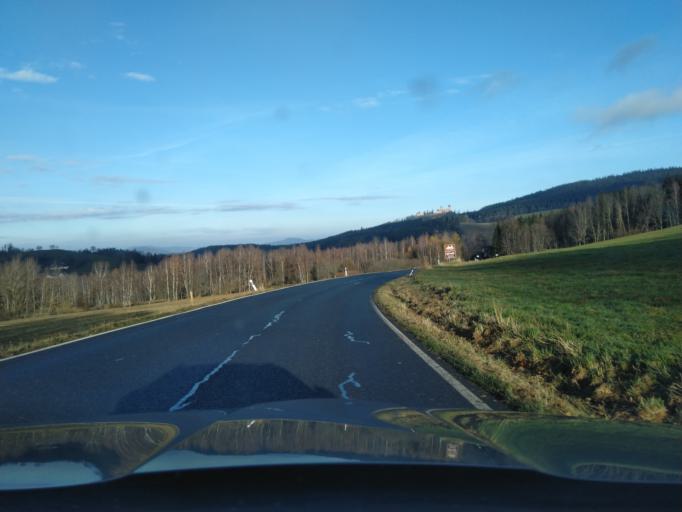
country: CZ
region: Plzensky
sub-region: Okres Klatovy
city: Kasperske Hory
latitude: 49.1416
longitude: 13.5739
